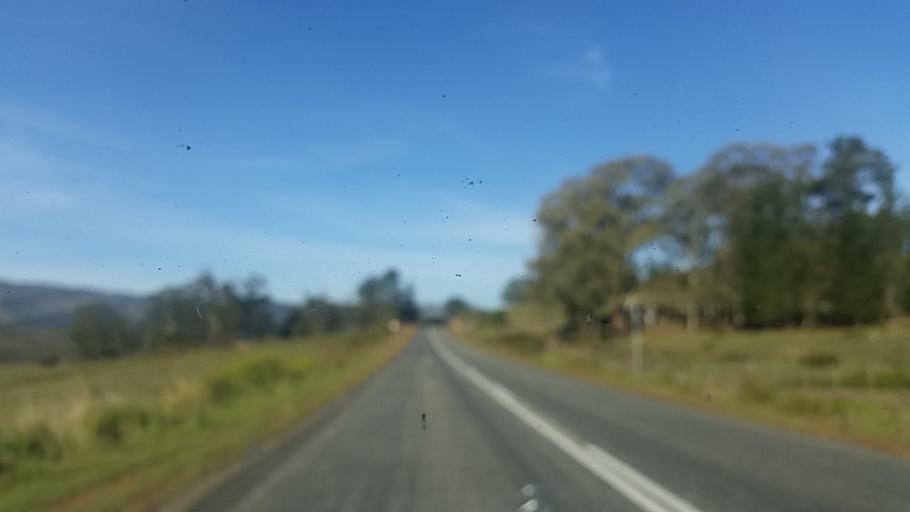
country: ZA
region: Western Cape
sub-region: Eden District Municipality
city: Knysna
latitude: -33.7736
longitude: 22.9151
